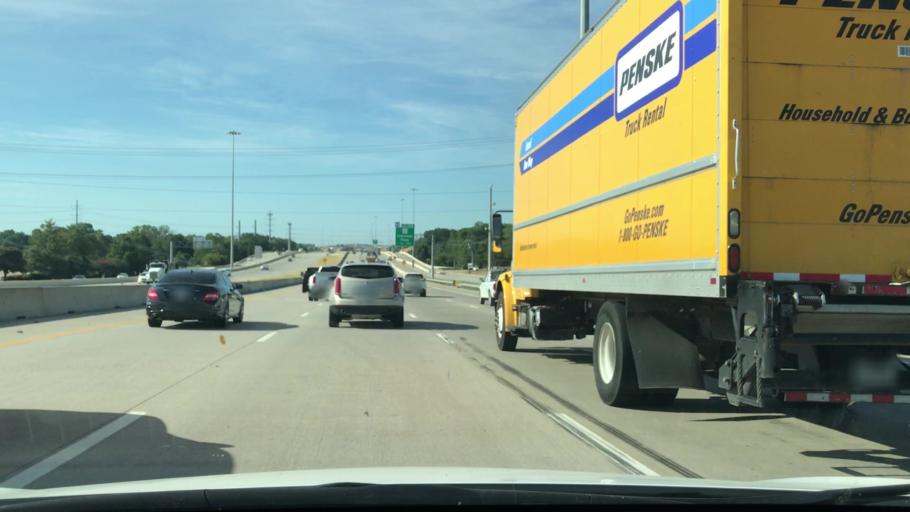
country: US
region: Texas
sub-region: Collin County
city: McKinney
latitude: 33.1907
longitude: -96.6373
